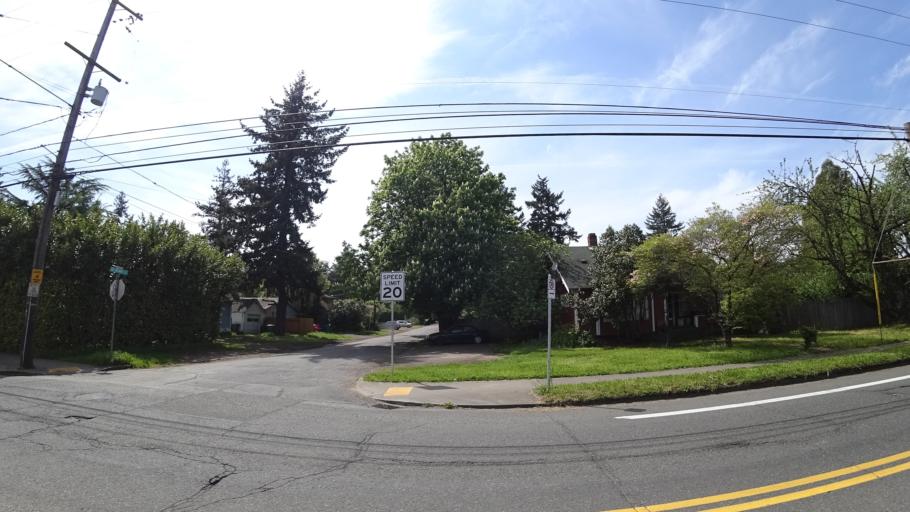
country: US
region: Oregon
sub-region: Multnomah County
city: Lents
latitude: 45.4763
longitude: -122.6088
